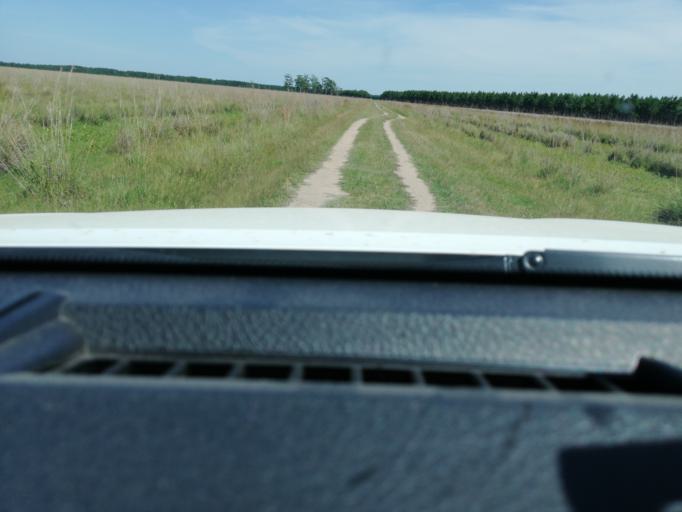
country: AR
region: Corrientes
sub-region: Departamento de San Miguel
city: San Miguel
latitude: -28.0412
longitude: -57.4601
